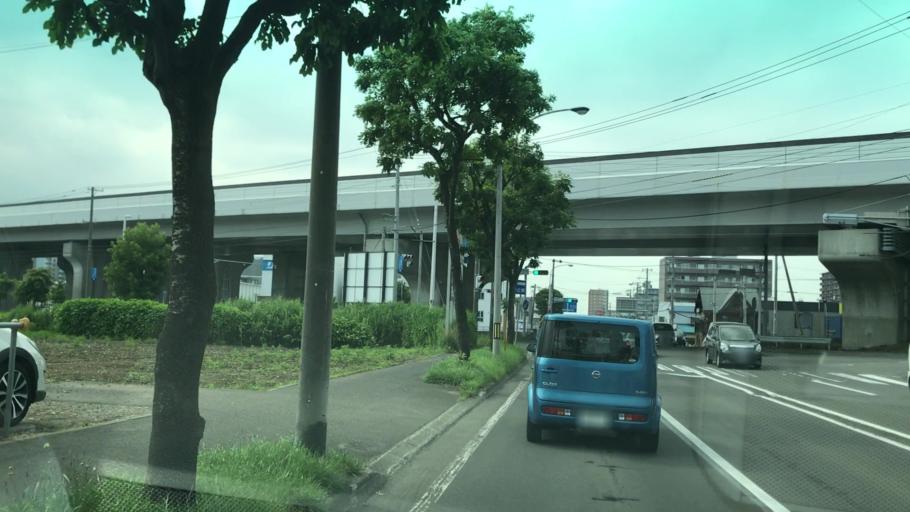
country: JP
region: Hokkaido
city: Sapporo
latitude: 43.0927
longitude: 141.2849
